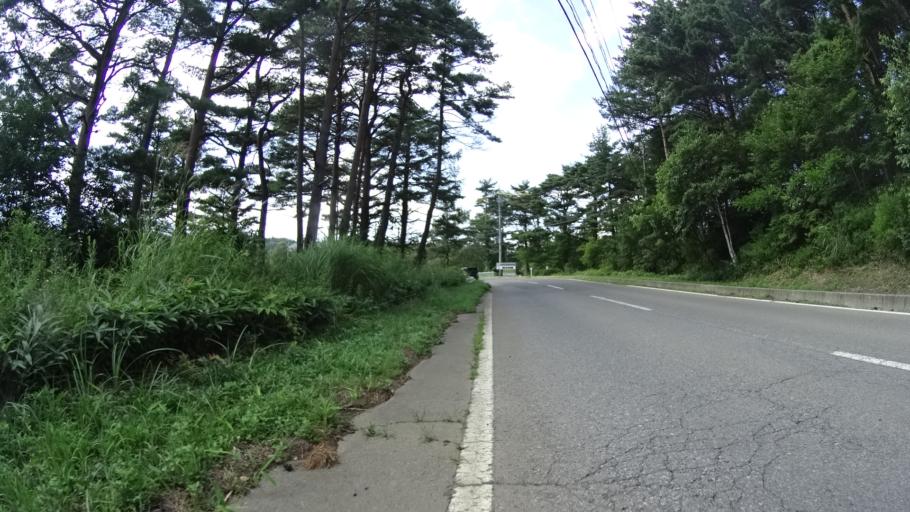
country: JP
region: Nagano
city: Saku
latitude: 36.0580
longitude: 138.4431
